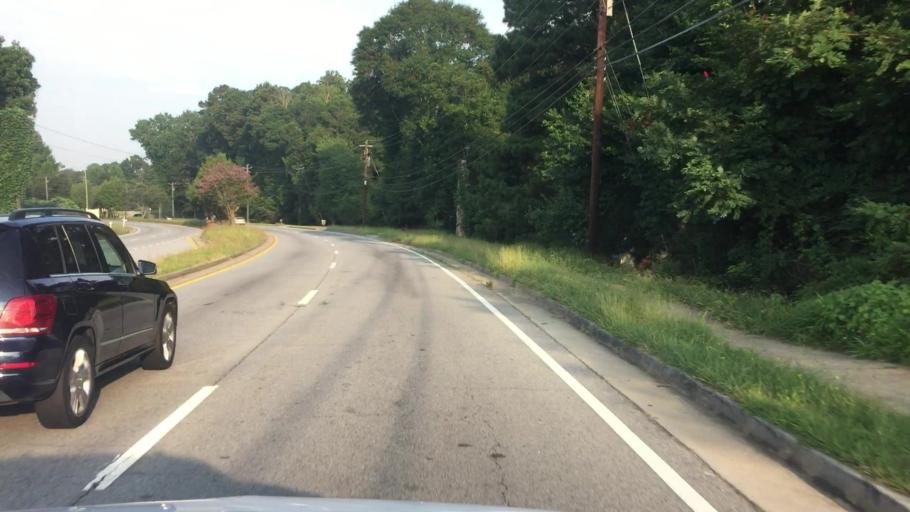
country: US
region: Georgia
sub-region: DeKalb County
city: Panthersville
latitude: 33.6840
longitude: -84.2384
